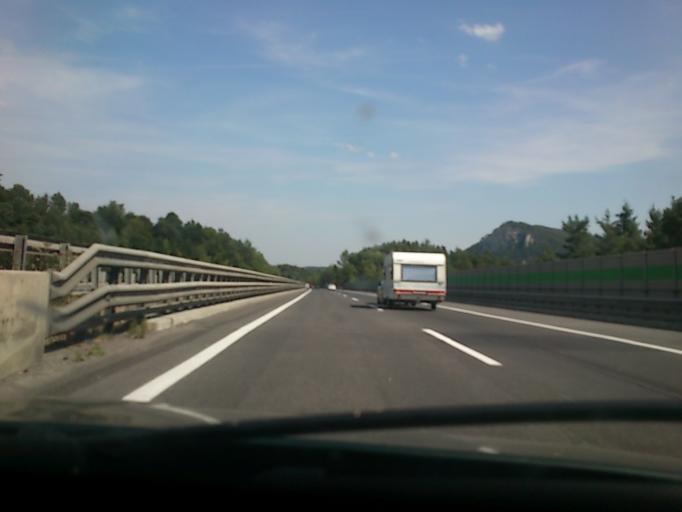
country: AT
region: Lower Austria
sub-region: Politischer Bezirk Neunkirchen
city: Warth
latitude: 47.6623
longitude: 16.1260
